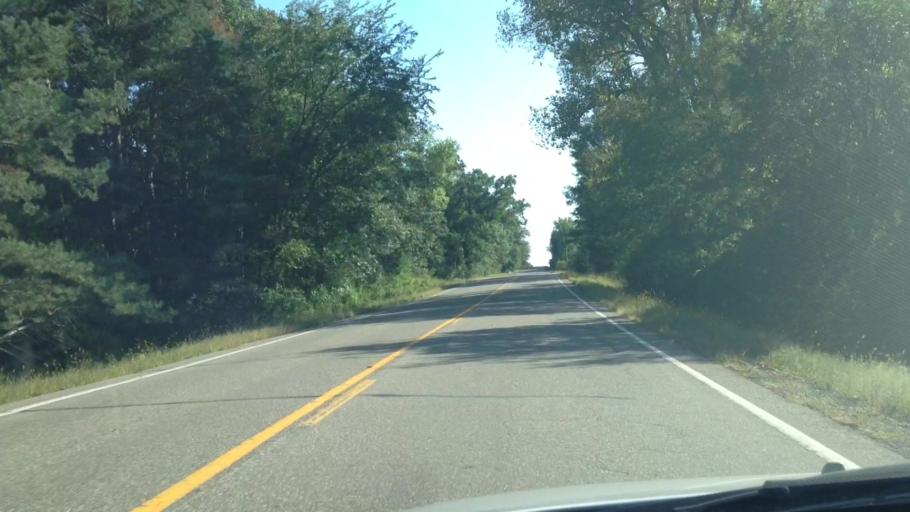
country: US
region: Minnesota
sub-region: Washington County
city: Stillwater
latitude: 45.1160
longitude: -92.8129
